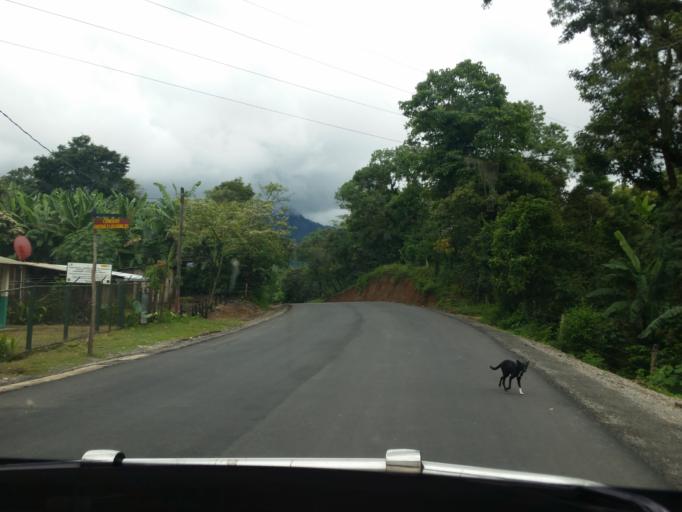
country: NI
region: Jinotega
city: Jinotega
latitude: 13.1481
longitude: -85.9357
